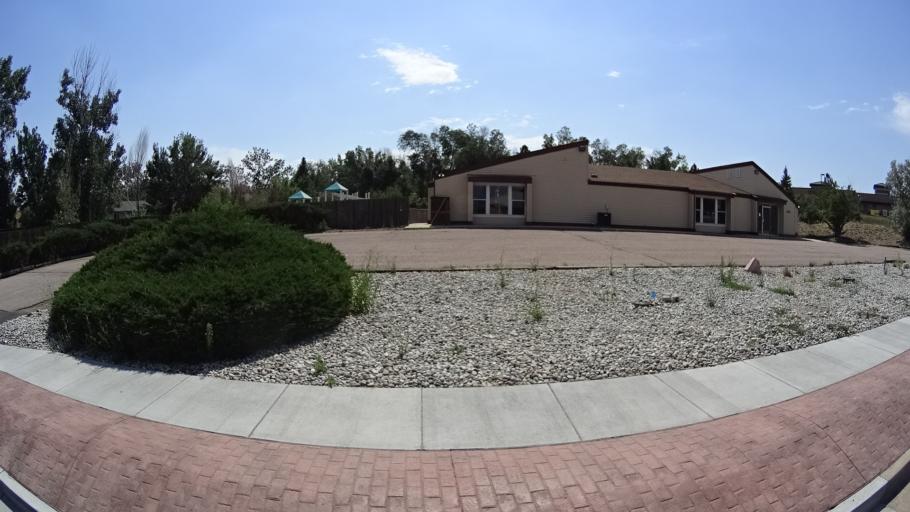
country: US
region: Colorado
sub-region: El Paso County
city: Colorado Springs
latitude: 38.9262
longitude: -104.7925
